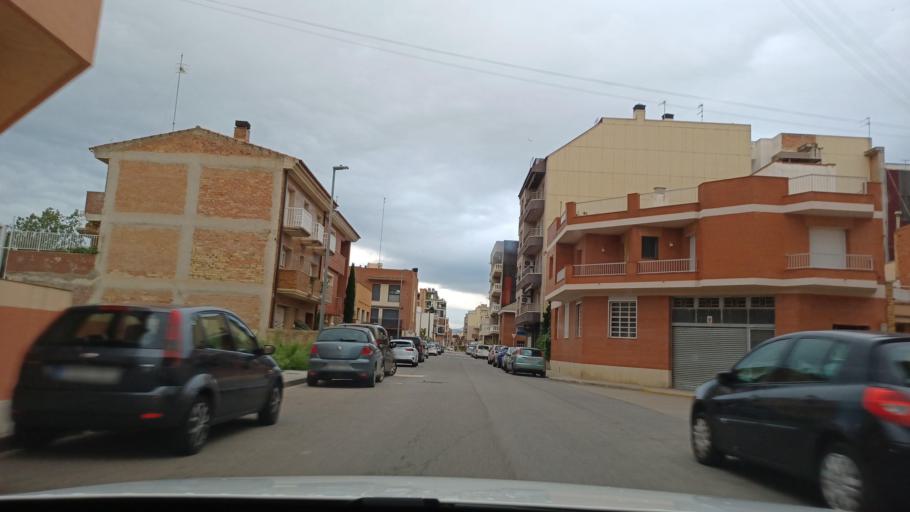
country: ES
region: Catalonia
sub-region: Provincia de Tarragona
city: Amposta
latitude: 40.7042
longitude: 0.5777
